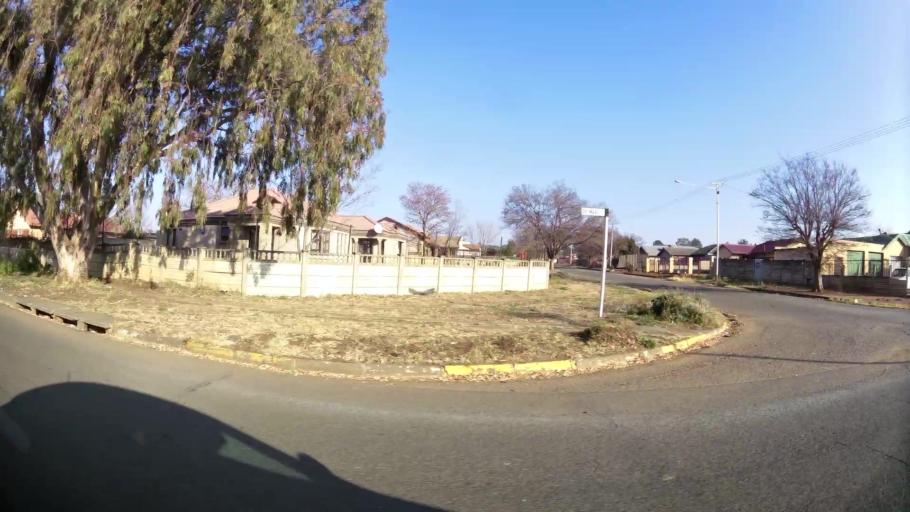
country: ZA
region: Orange Free State
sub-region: Mangaung Metropolitan Municipality
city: Bloemfontein
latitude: -29.1484
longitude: 26.2136
